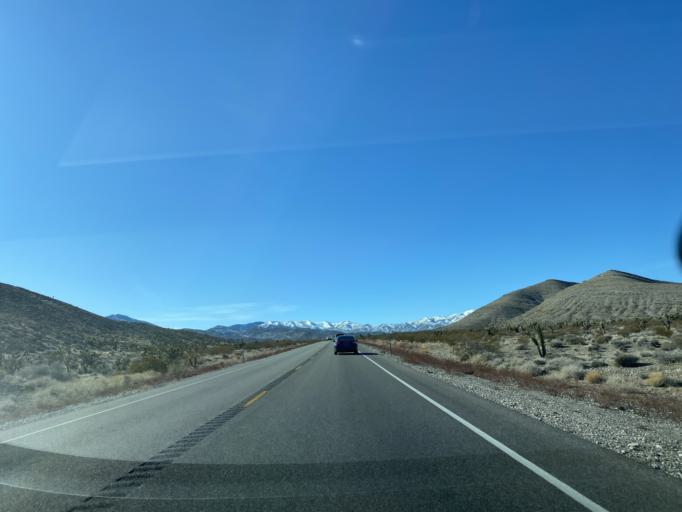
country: US
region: Nevada
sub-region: Clark County
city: Summerlin South
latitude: 36.2896
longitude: -115.4294
